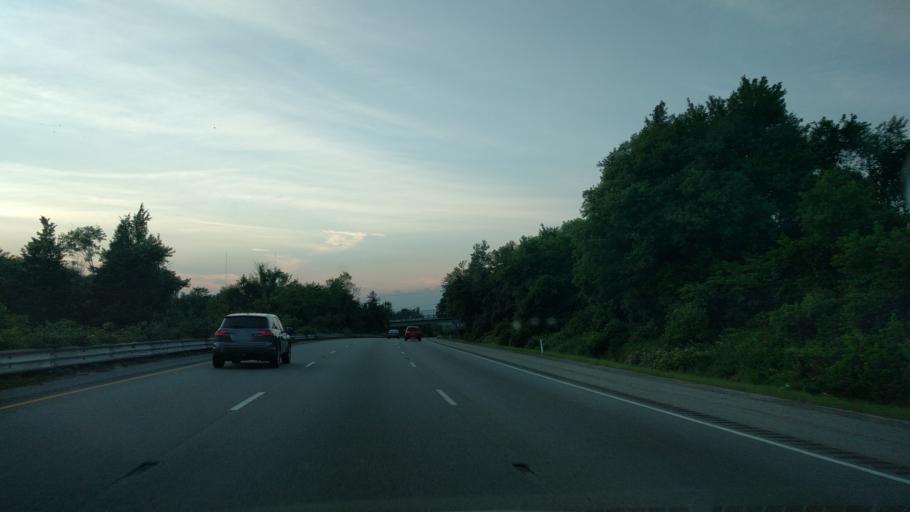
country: US
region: Massachusetts
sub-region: Bristol County
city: Ocean Grove
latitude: 41.7168
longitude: -71.1814
